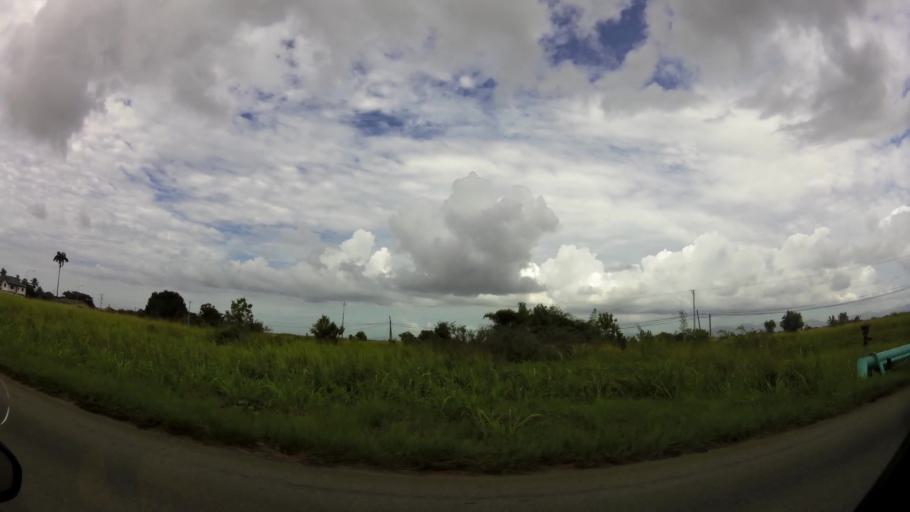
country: TT
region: Couva-Tabaquite-Talparo
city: Couva
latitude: 10.4531
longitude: -61.4372
